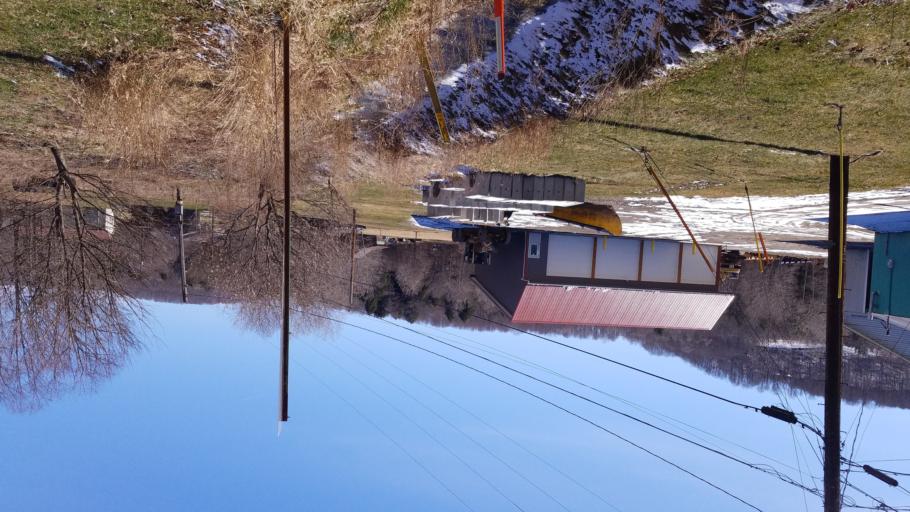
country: US
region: New York
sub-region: Allegany County
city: Wellsville
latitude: 41.9858
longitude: -77.8612
